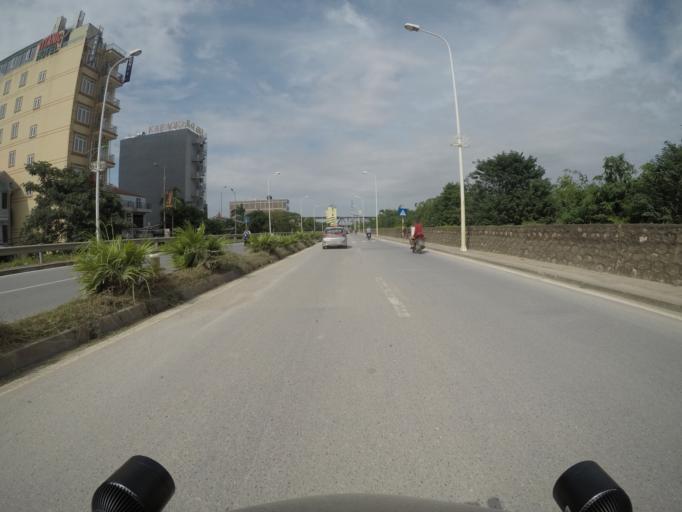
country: VN
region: Ha Noi
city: Tay Ho
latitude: 21.0905
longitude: 105.7901
